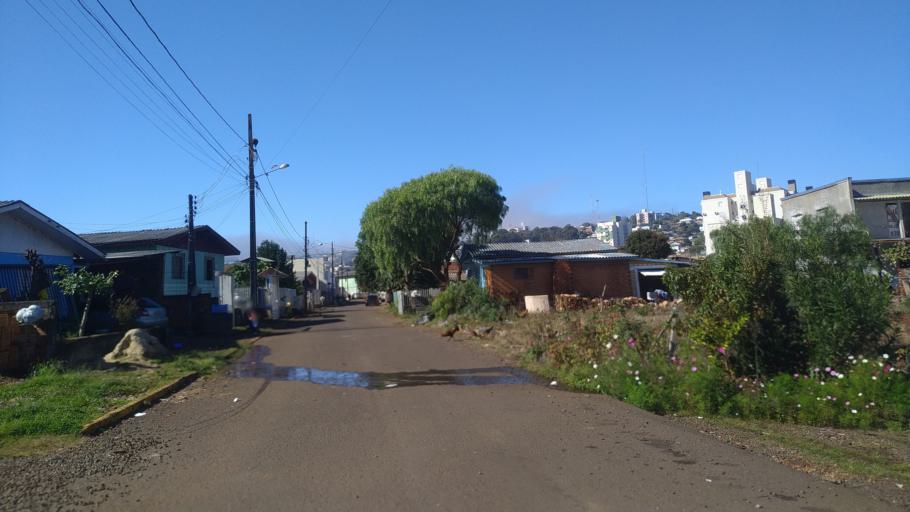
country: BR
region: Santa Catarina
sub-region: Chapeco
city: Chapeco
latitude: -27.1134
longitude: -52.6011
